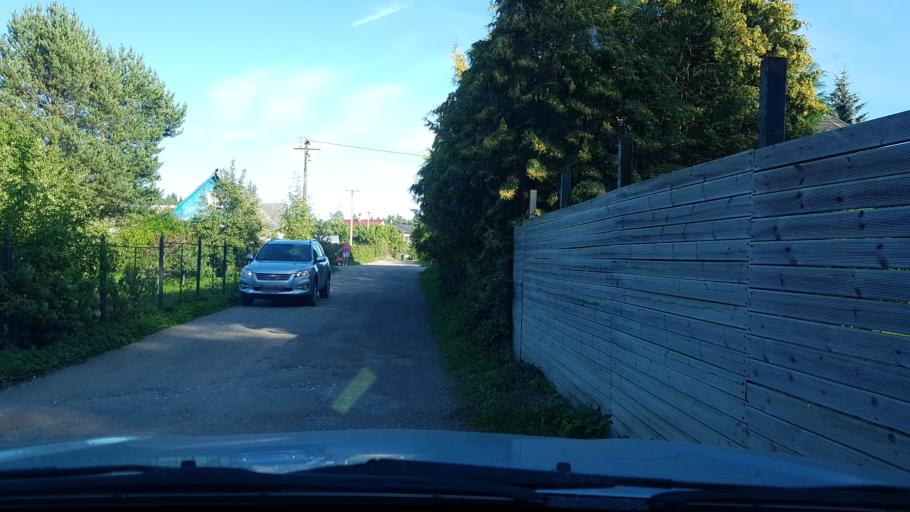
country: EE
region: Ida-Virumaa
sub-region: Narva-Joesuu linn
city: Narva-Joesuu
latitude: 59.4460
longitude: 28.0723
